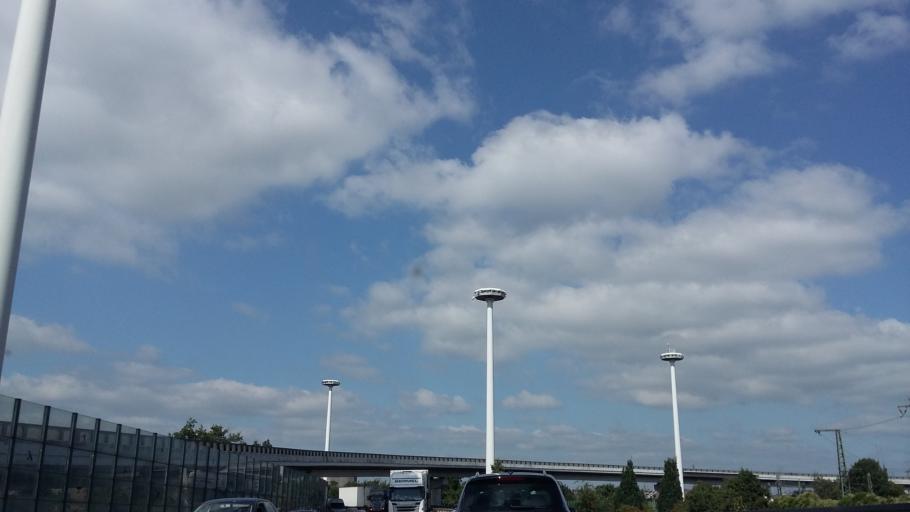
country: DE
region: Bremen
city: Bremen
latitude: 53.0861
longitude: 8.7962
